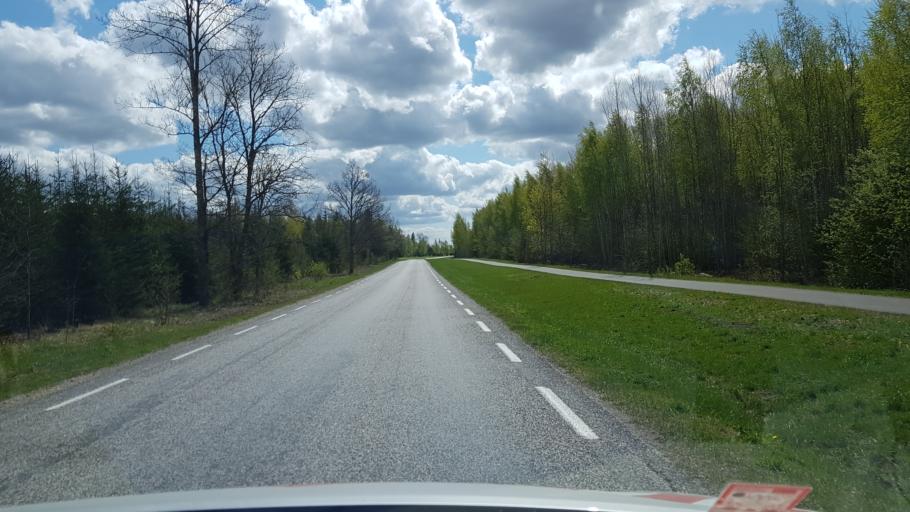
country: EE
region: Jogevamaa
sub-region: Poltsamaa linn
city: Poltsamaa
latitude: 58.6926
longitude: 25.9450
